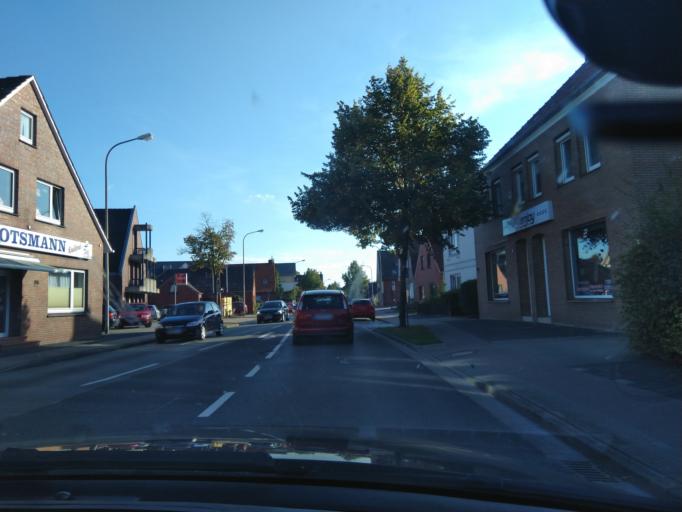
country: DE
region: Lower Saxony
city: Leer
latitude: 53.2434
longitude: 7.4569
